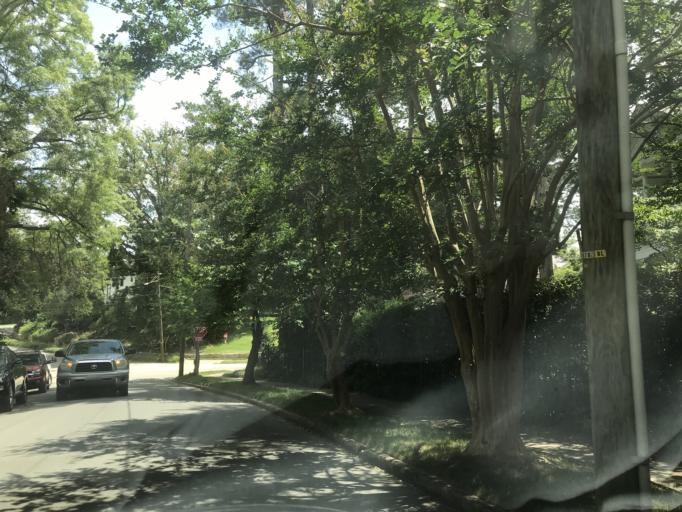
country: US
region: North Carolina
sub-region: Wake County
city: West Raleigh
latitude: 35.8017
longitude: -78.6519
